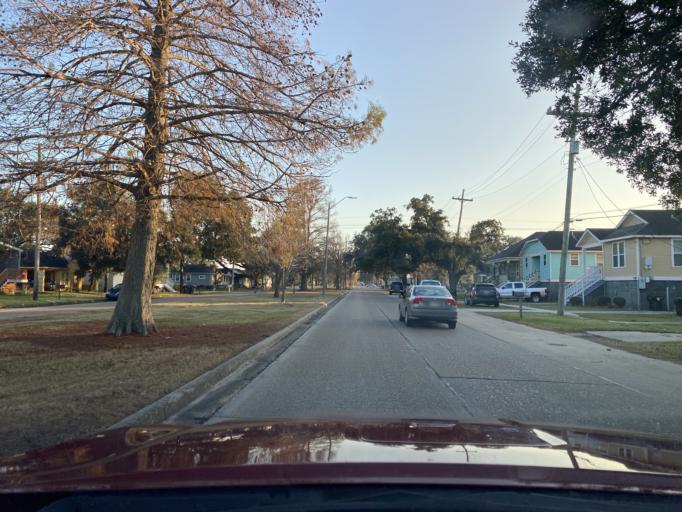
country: US
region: Louisiana
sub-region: Orleans Parish
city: New Orleans
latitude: 30.0247
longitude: -90.0521
